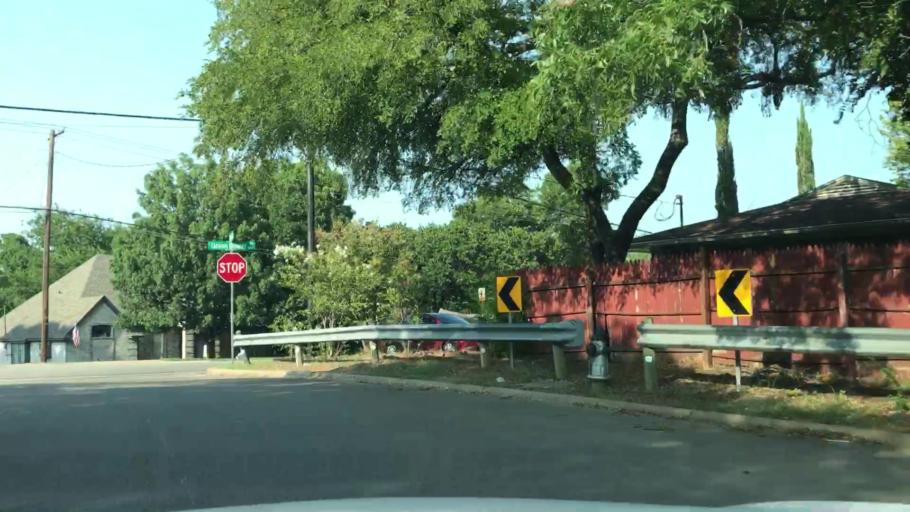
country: US
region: Texas
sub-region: Dallas County
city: Irving
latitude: 32.8235
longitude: -96.9250
